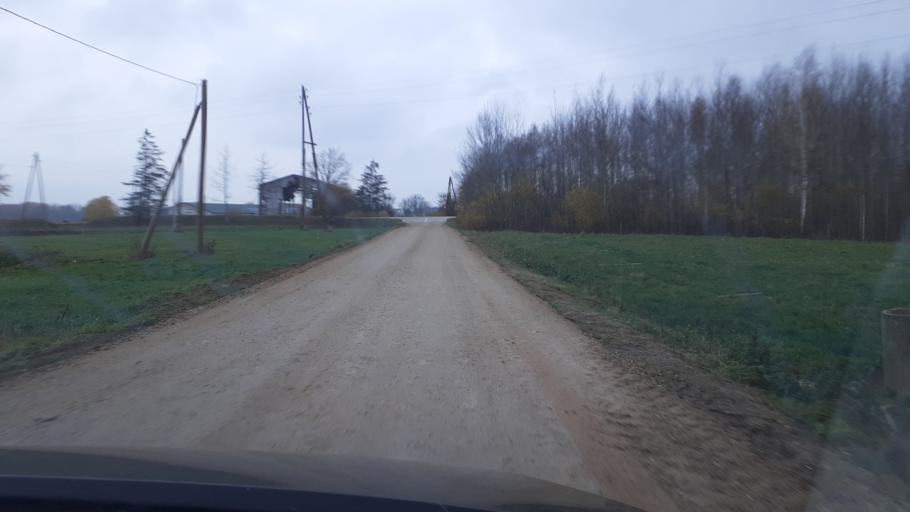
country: LV
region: Talsu Rajons
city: Sabile
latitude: 56.9417
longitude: 22.4205
